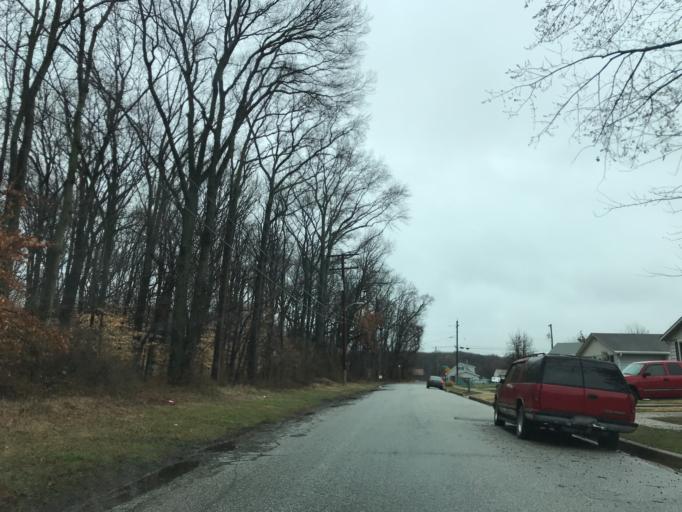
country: US
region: Maryland
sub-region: Baltimore County
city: Edgemere
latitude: 39.2291
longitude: -76.4419
